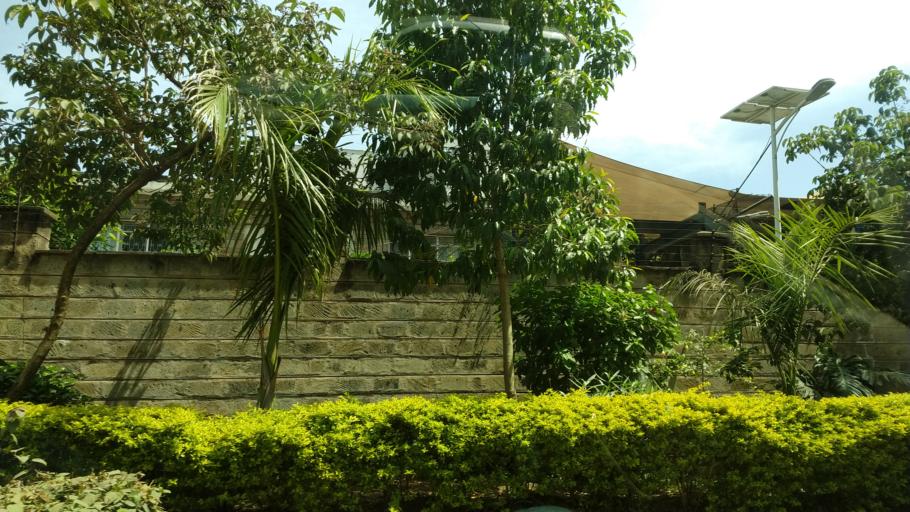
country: KE
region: Nairobi Area
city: Nairobi
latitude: -1.2956
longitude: 36.7863
